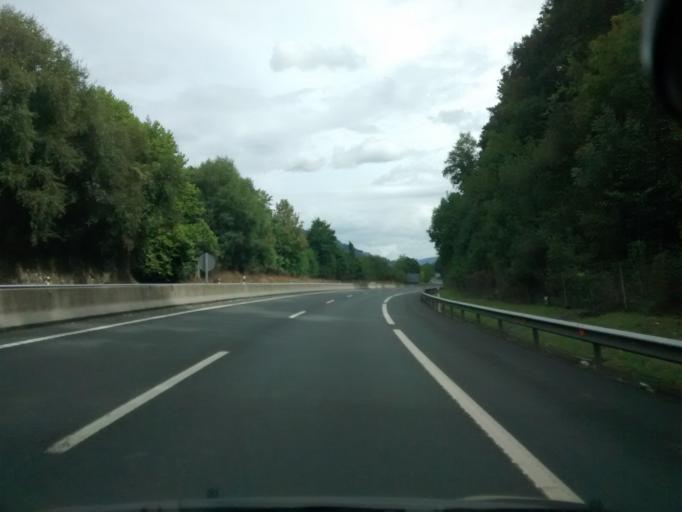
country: ES
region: Basque Country
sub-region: Bizkaia
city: Ermua
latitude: 43.1783
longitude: -2.4892
